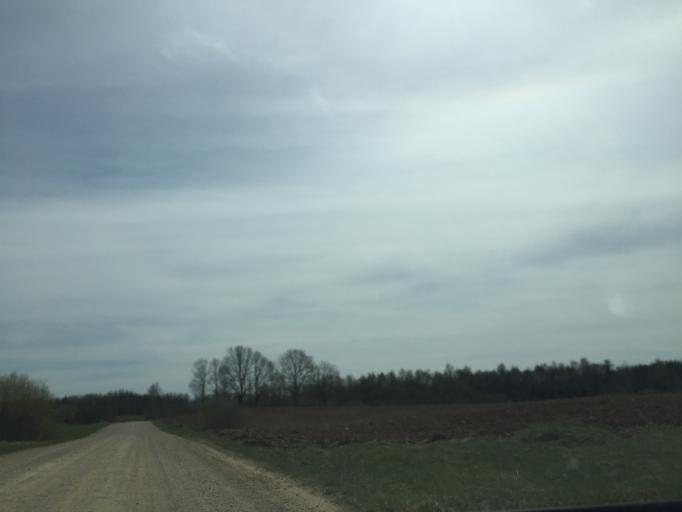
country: LV
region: Ludzas Rajons
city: Ludza
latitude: 56.5818
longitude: 27.5448
